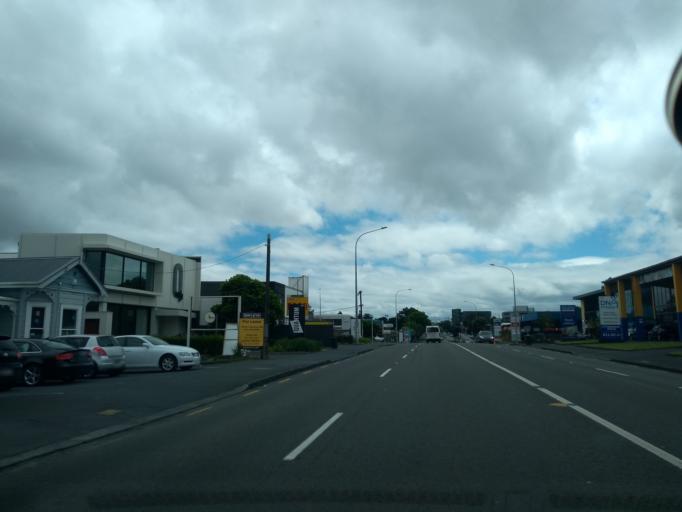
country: NZ
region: Auckland
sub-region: Auckland
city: Tamaki
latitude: -36.9063
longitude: 174.8109
